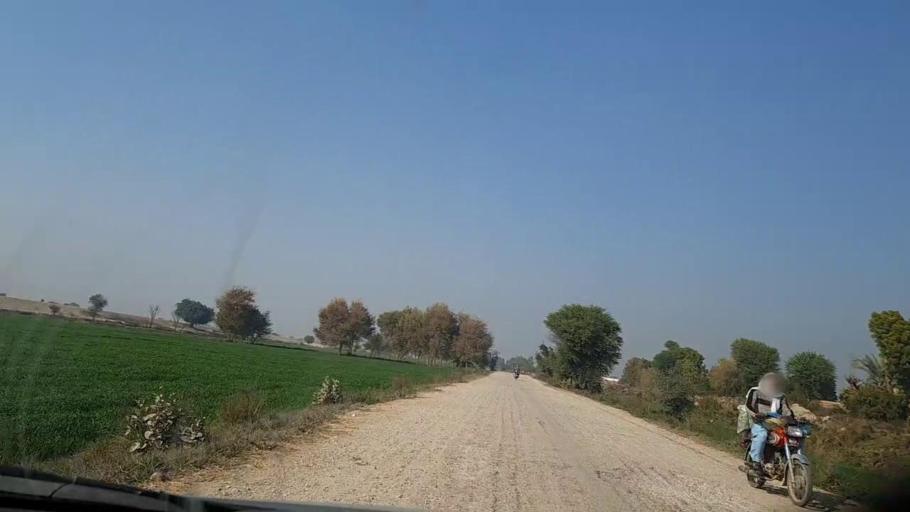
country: PK
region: Sindh
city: Moro
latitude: 26.7347
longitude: 67.9199
